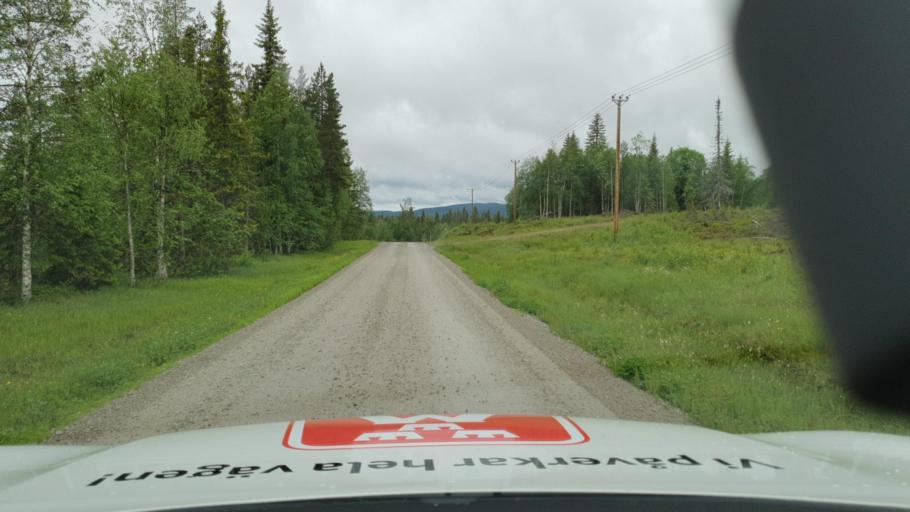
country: SE
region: Vaesterbotten
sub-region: Dorotea Kommun
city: Dorotea
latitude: 63.9739
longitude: 16.8464
